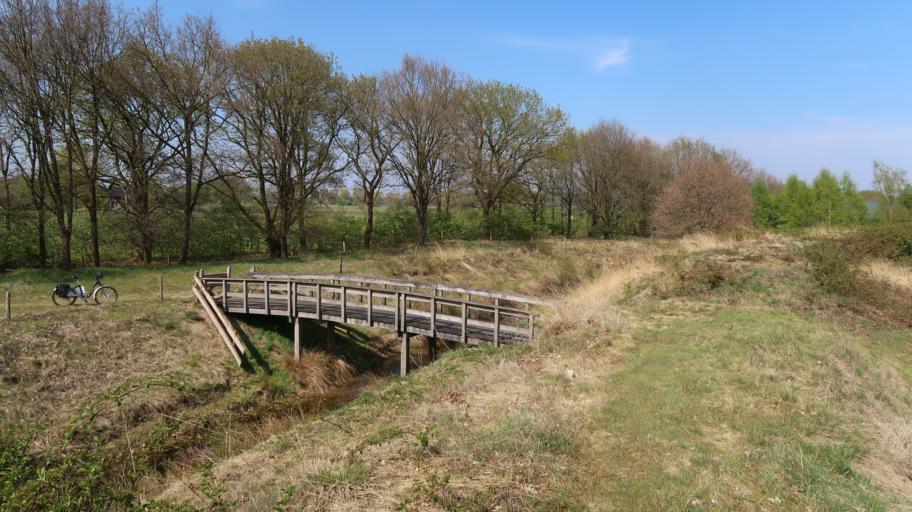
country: DE
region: Lower Saxony
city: Emlichheim
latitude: 52.6673
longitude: 6.8208
